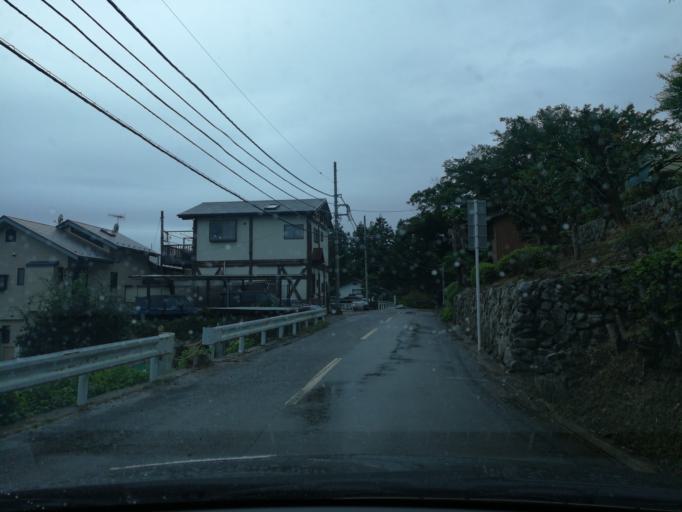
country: JP
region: Yamanashi
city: Uenohara
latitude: 35.6113
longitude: 139.2224
